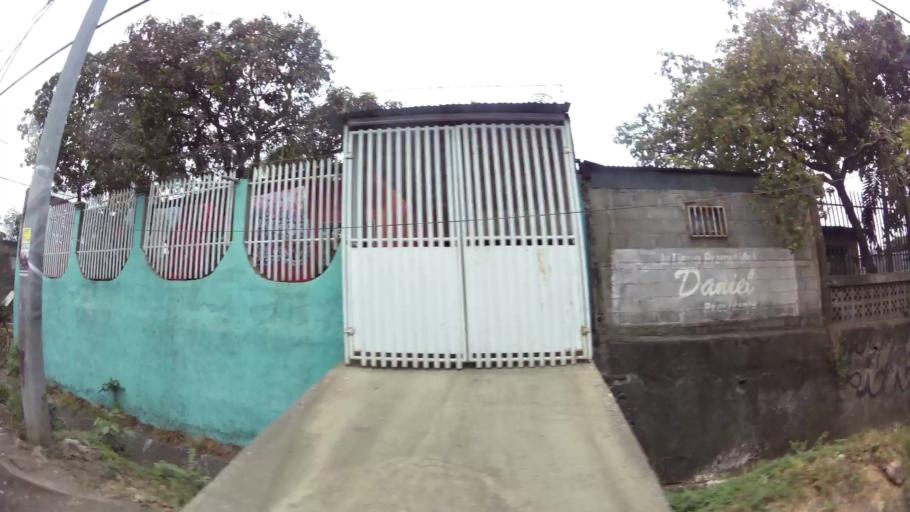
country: NI
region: Managua
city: Managua
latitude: 12.1221
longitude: -86.2159
